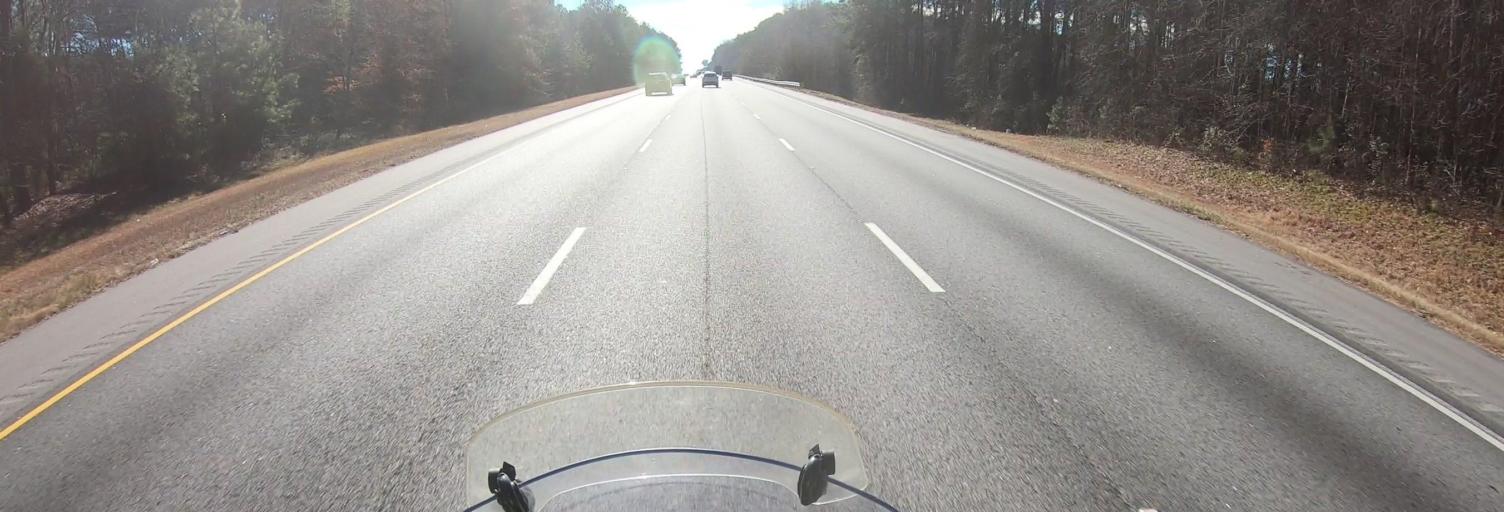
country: US
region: Georgia
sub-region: Henry County
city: McDonough
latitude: 33.3934
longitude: -84.1532
